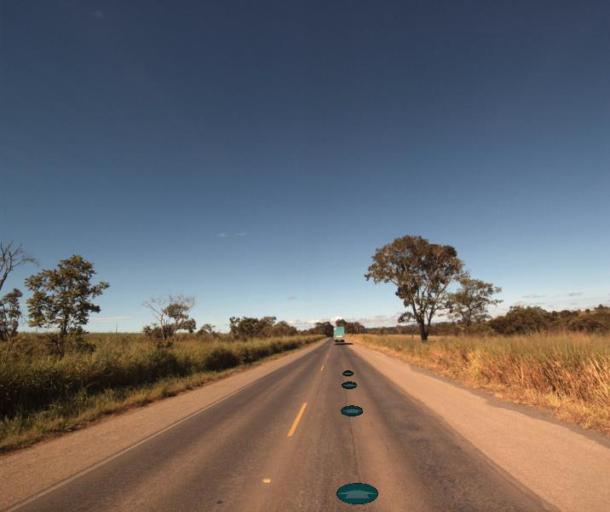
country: BR
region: Goias
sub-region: Itapaci
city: Itapaci
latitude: -14.9687
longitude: -49.3888
